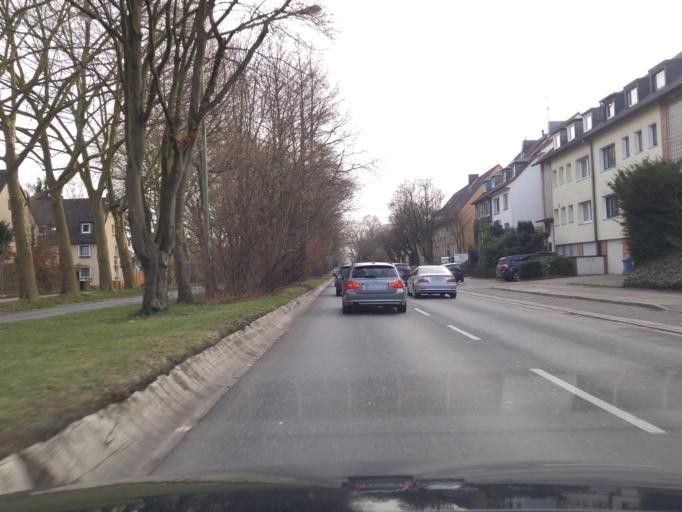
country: DE
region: North Rhine-Westphalia
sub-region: Regierungsbezirk Dusseldorf
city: Essen
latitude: 51.4393
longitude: 7.0384
